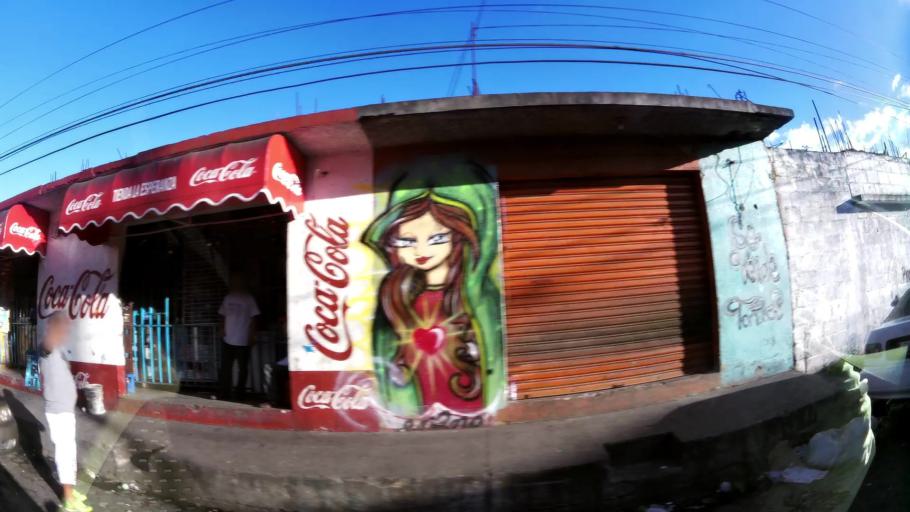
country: GT
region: Guatemala
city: Guatemala City
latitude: 14.6155
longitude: -90.5272
